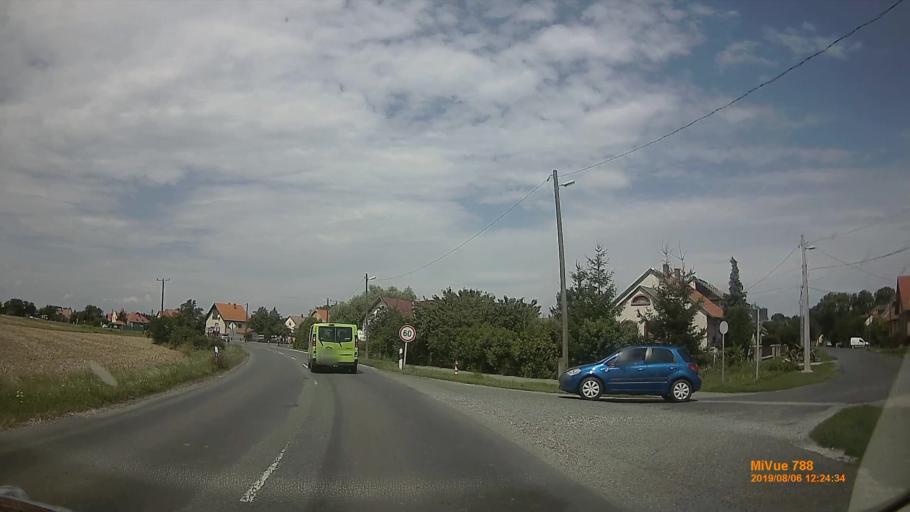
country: HU
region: Vas
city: Taplanszentkereszt
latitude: 47.1938
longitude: 16.6971
